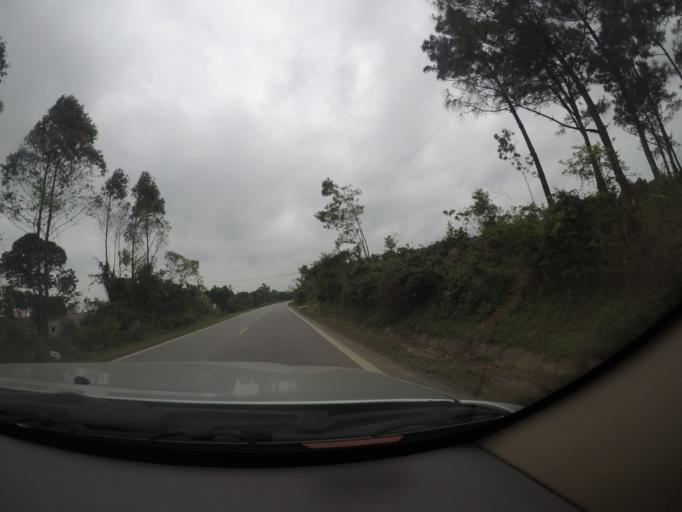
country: VN
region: Quang Binh
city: Quan Hau
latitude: 17.3692
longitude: 106.6213
